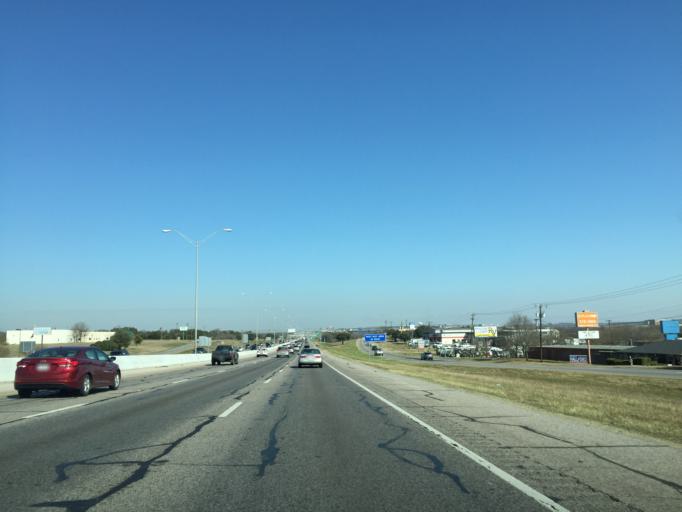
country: US
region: Texas
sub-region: Williamson County
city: Round Rock
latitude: 30.5424
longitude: -97.6922
